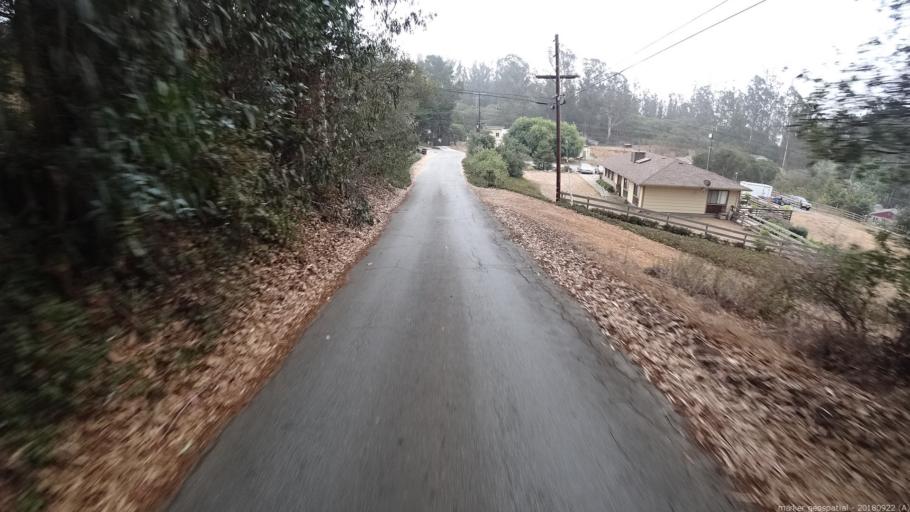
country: US
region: California
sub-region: Monterey County
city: Prunedale
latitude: 36.7920
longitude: -121.6754
